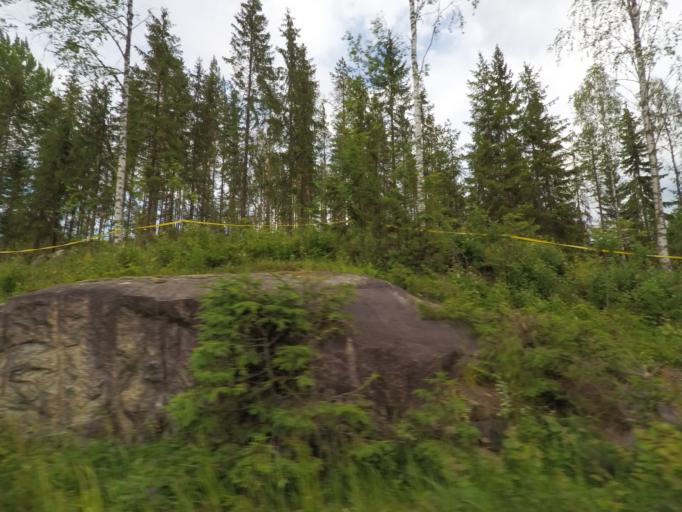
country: FI
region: Paijanne Tavastia
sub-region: Lahti
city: Hollola
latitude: 60.8325
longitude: 25.4910
